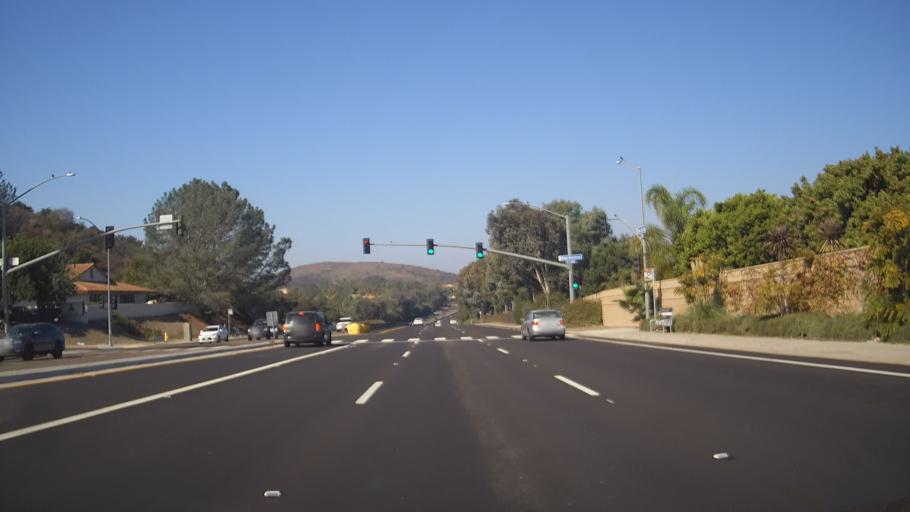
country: US
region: California
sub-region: San Diego County
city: Poway
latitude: 33.0000
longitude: -117.0863
